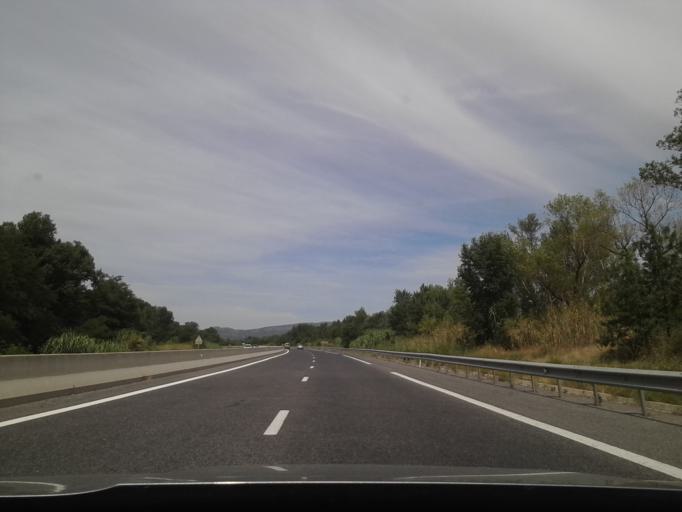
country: FR
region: Languedoc-Roussillon
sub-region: Departement des Pyrenees-Orientales
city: Corneilla-la-Riviere
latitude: 42.6875
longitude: 2.7328
